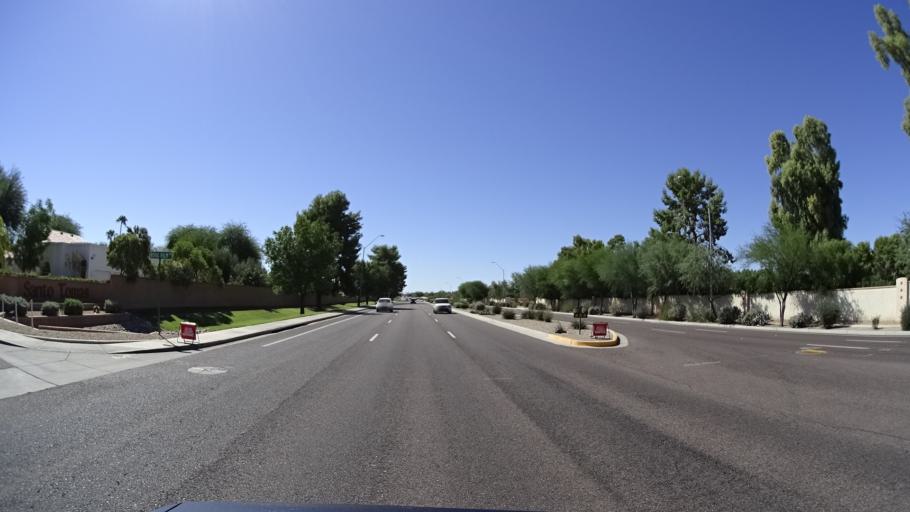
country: US
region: Arizona
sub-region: Maricopa County
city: Paradise Valley
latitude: 33.5564
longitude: -111.9260
